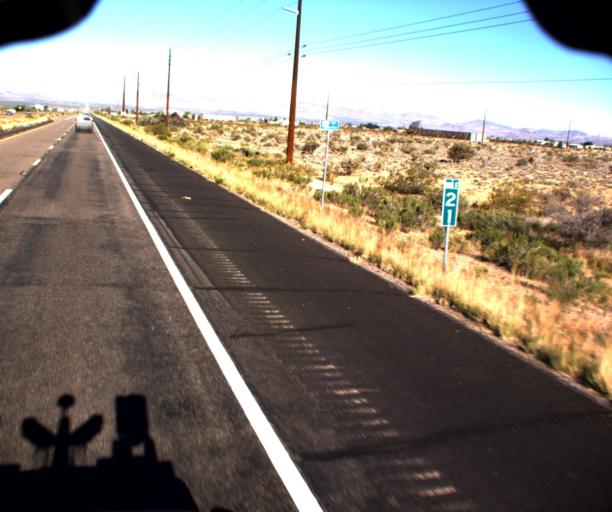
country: US
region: Arizona
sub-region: Mohave County
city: Golden Valley
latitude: 35.2230
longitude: -114.2325
